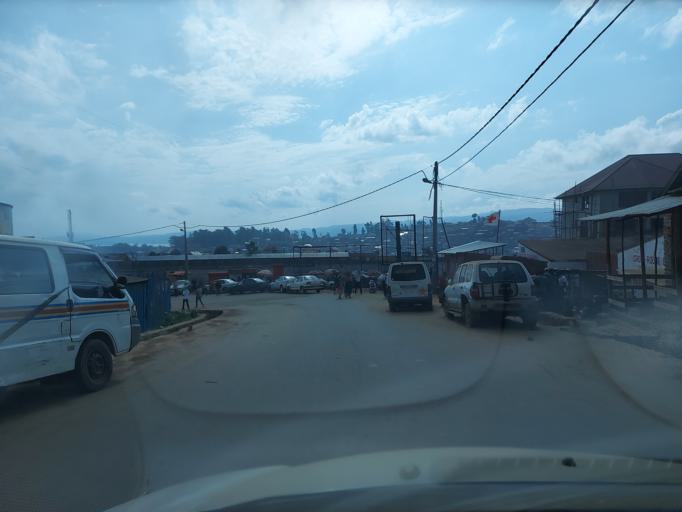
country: CD
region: South Kivu
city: Bukavu
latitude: -2.5184
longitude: 28.8511
